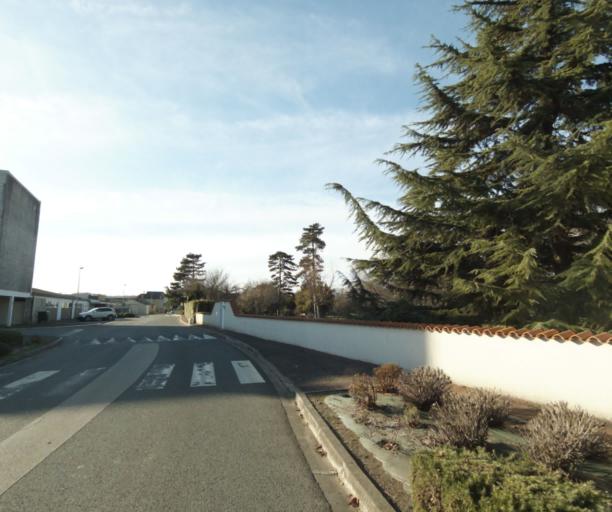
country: FR
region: Poitou-Charentes
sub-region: Departement de la Charente-Maritime
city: Burie
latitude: 45.7766
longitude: -0.4157
